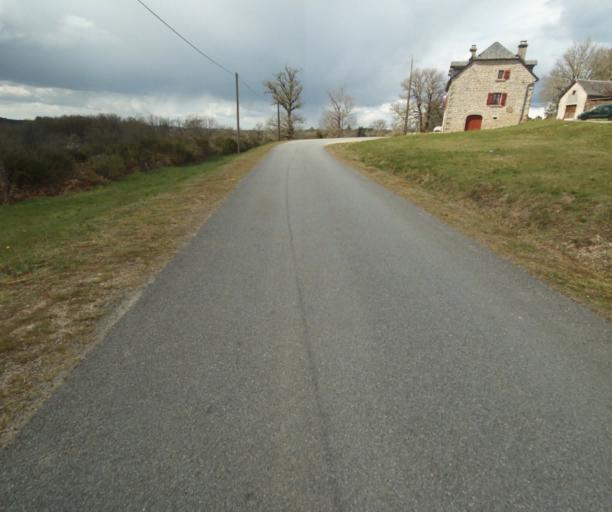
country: FR
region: Limousin
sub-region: Departement de la Correze
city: Correze
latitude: 45.3114
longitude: 1.9323
